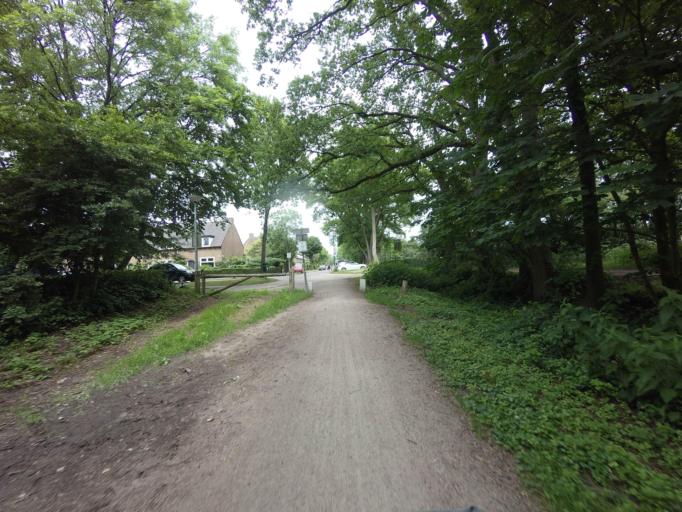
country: NL
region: North Holland
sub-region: Gemeente Laren
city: Laren
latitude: 52.2453
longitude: 5.2380
